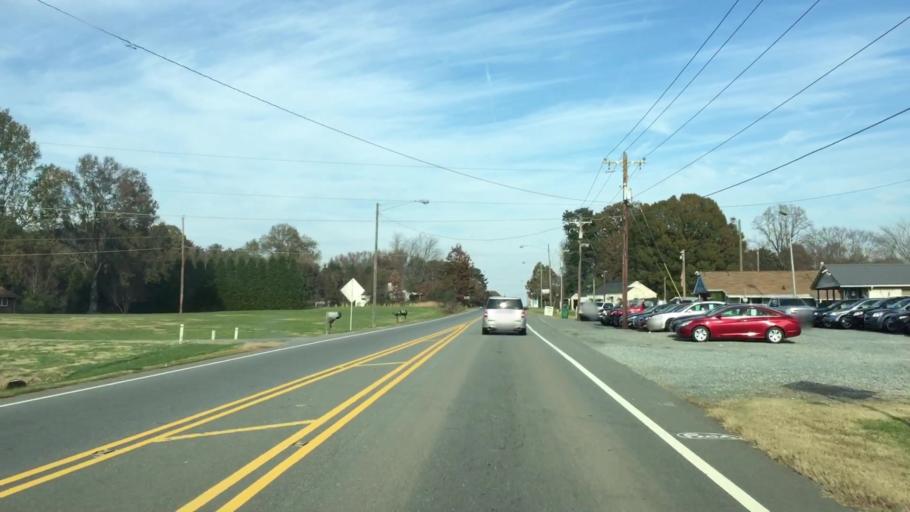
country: US
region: North Carolina
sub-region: Forsyth County
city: Walkertown
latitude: 36.1534
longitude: -80.1491
